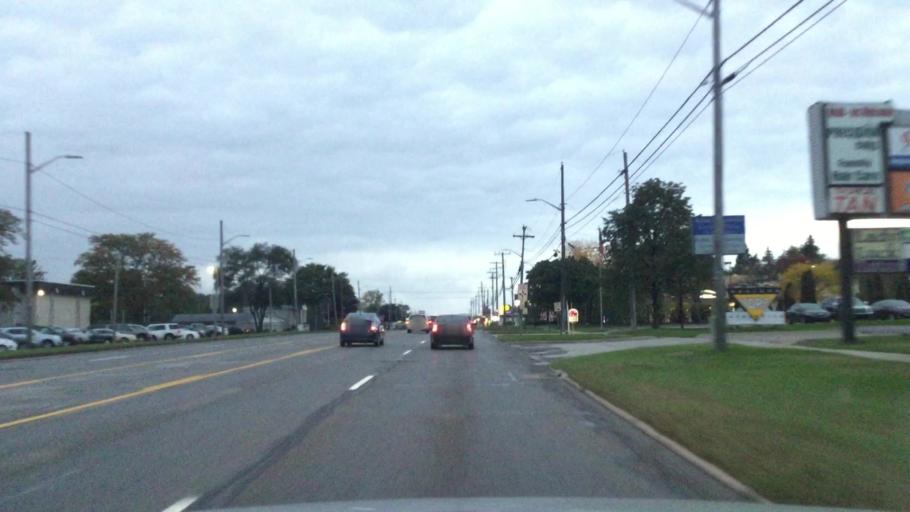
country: US
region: Michigan
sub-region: Oakland County
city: Waterford
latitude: 42.6603
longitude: -83.3930
